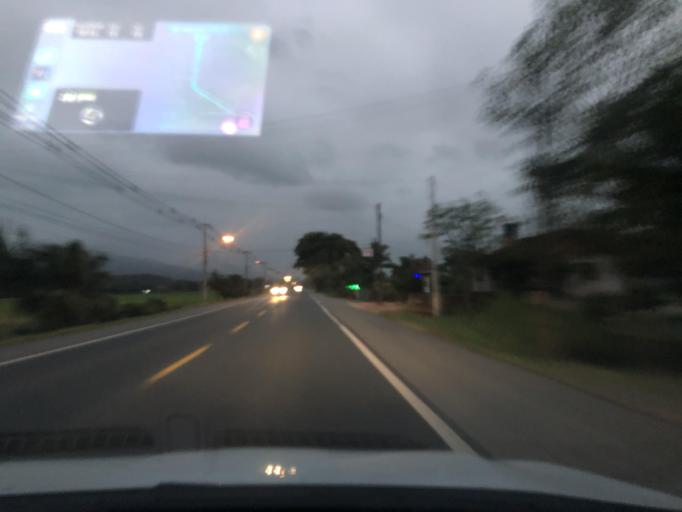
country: BR
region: Santa Catarina
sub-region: Jaragua Do Sul
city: Jaragua do Sul
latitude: -26.6271
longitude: -49.0124
